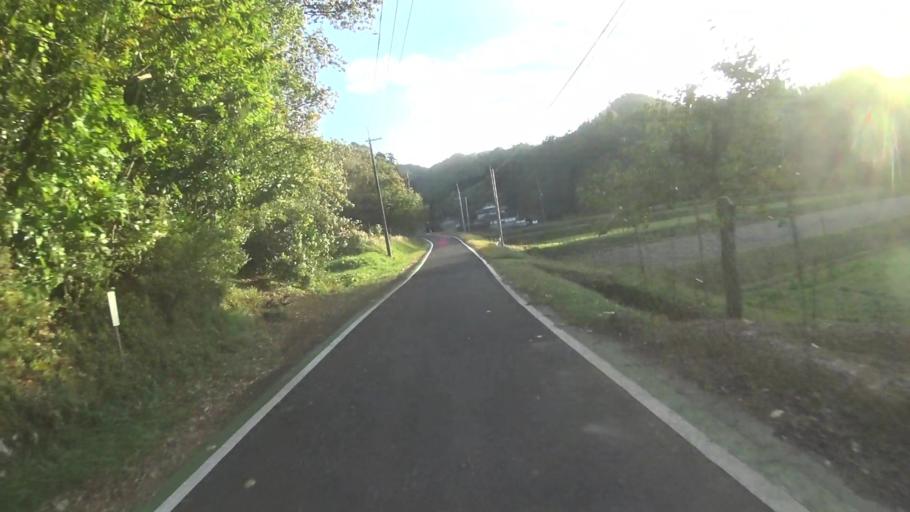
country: JP
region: Kyoto
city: Ayabe
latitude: 35.2790
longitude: 135.2501
